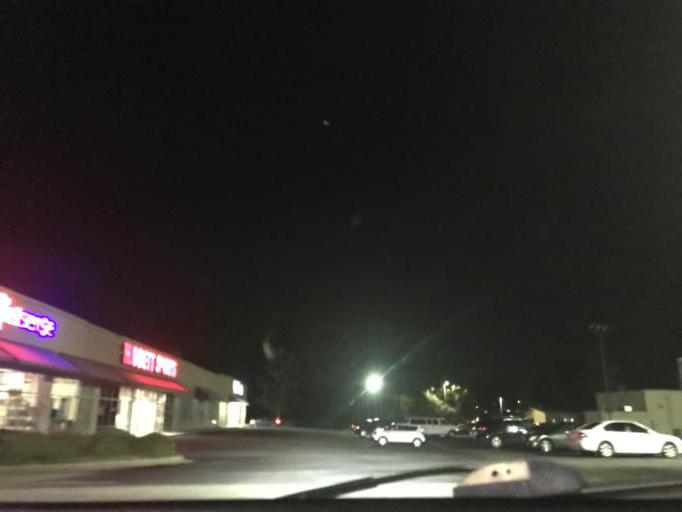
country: US
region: South Carolina
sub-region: Cherokee County
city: Gaffney
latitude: 35.0860
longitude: -81.6586
